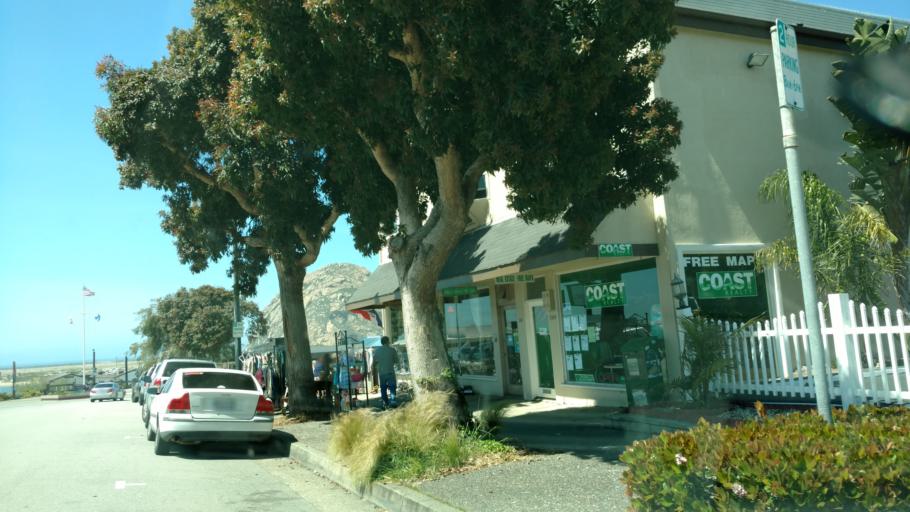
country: US
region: California
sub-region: San Luis Obispo County
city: Morro Bay
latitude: 35.3660
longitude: -120.8515
